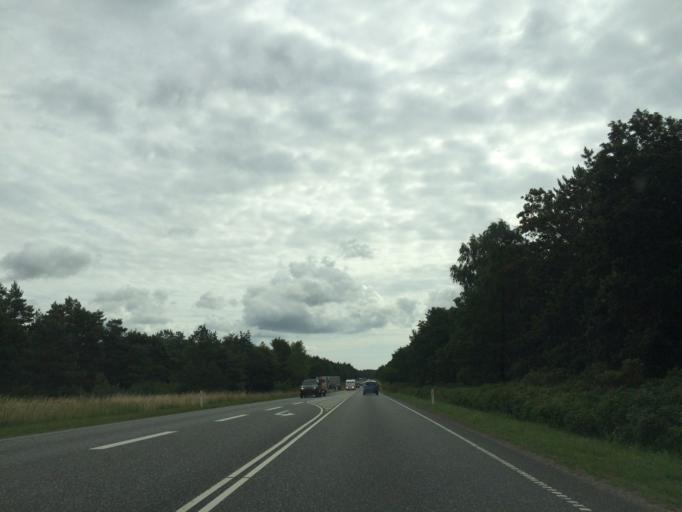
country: DK
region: Central Jutland
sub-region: Syddjurs Kommune
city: Ronde
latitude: 56.2936
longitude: 10.5916
